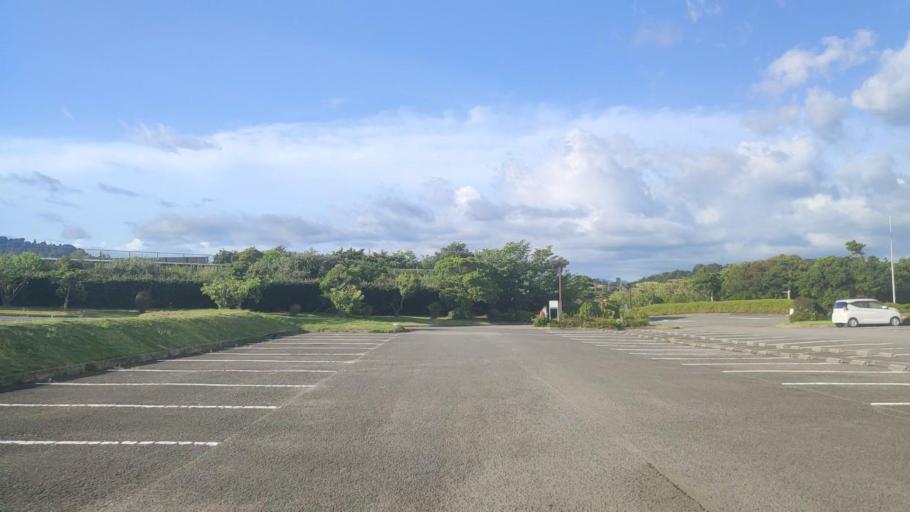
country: JP
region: Wakayama
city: Tanabe
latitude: 33.7689
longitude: 135.3014
